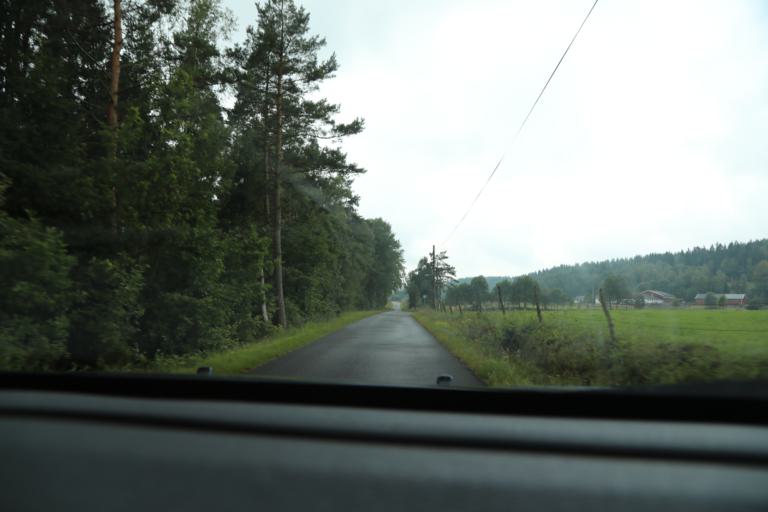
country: SE
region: Halland
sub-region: Falkenbergs Kommun
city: Falkenberg
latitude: 57.1136
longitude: 12.6826
